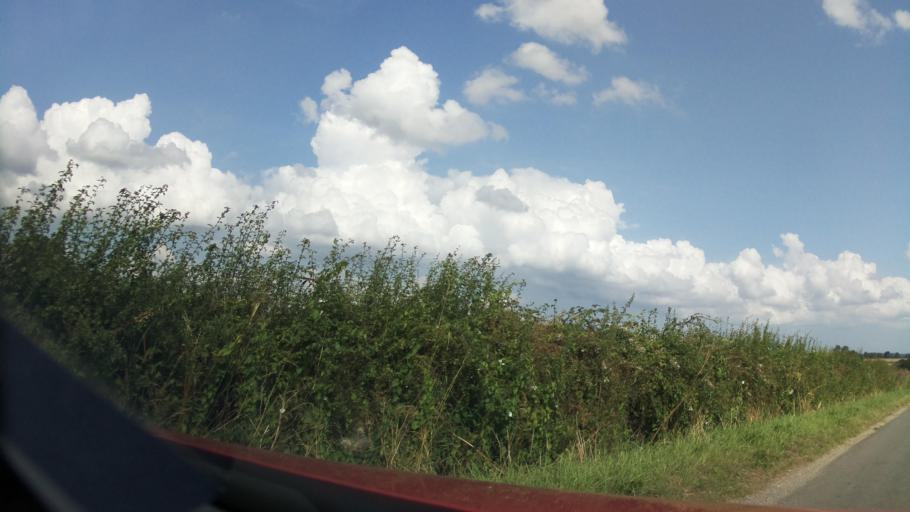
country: GB
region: England
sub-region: Wiltshire
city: Malmesbury
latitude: 51.5728
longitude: -2.1225
